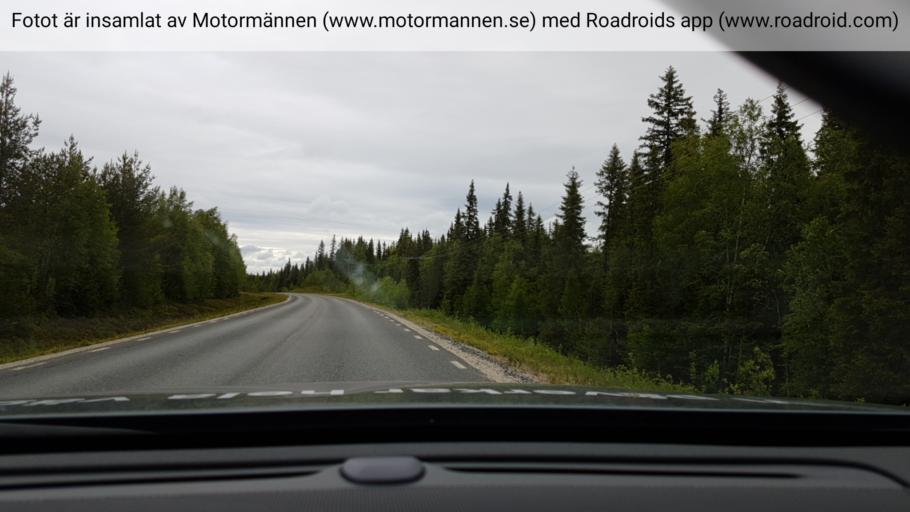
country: SE
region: Vaesterbotten
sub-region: Lycksele Kommun
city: Soderfors
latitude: 64.4752
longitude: 18.2382
